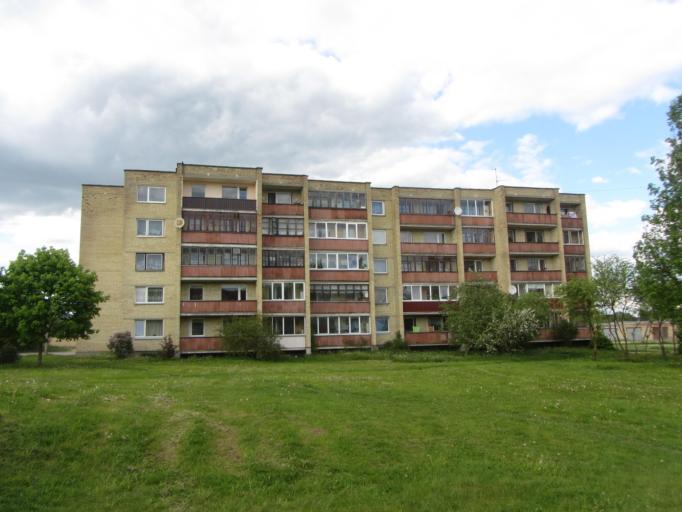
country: LT
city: Sirvintos
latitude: 55.0483
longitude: 24.9575
